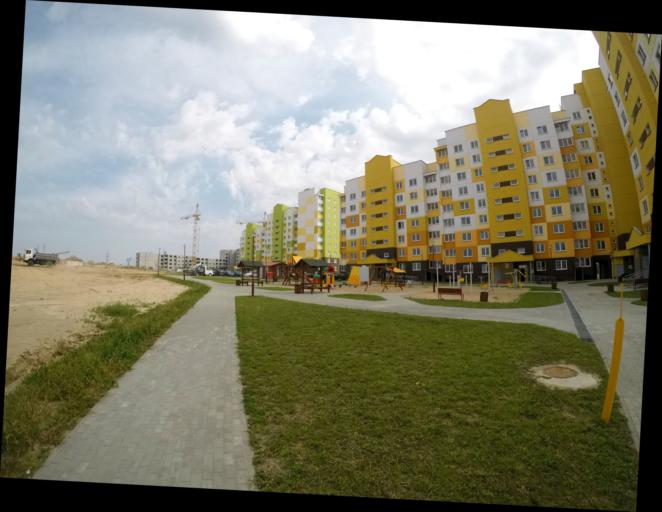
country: BY
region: Grodnenskaya
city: Hrodna
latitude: 53.7184
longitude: 23.8640
